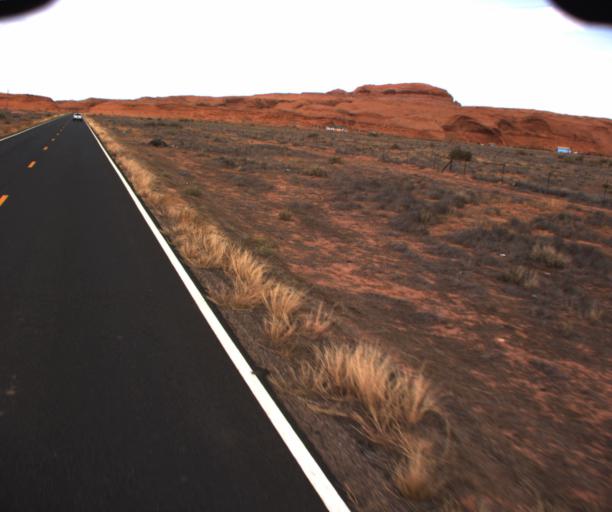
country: US
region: Arizona
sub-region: Apache County
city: Many Farms
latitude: 36.7579
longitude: -109.6481
